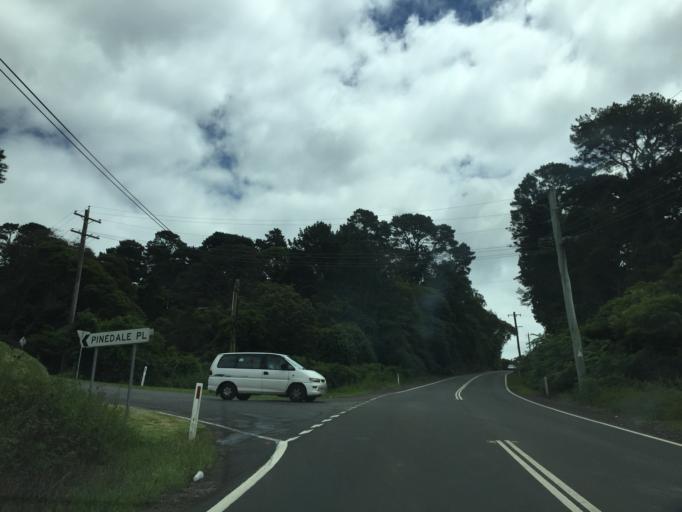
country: AU
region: New South Wales
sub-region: Hawkesbury
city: Richmond
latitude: -33.5226
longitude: 150.6280
